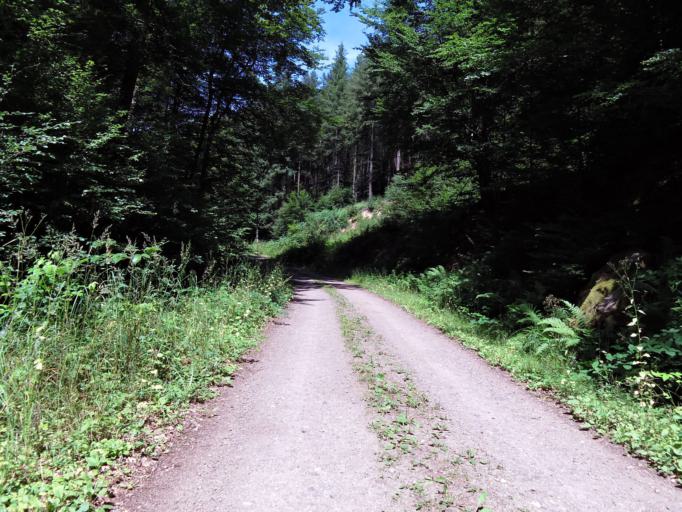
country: DE
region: Rheinland-Pfalz
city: Wilgartswiesen
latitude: 49.2645
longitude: 7.8796
